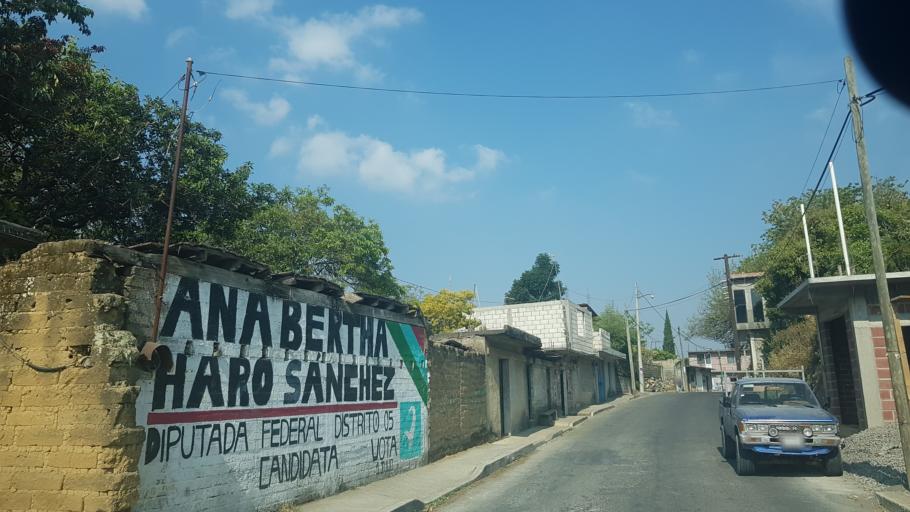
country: MX
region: Morelos
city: Hueyapan
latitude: 18.8879
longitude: -98.6827
